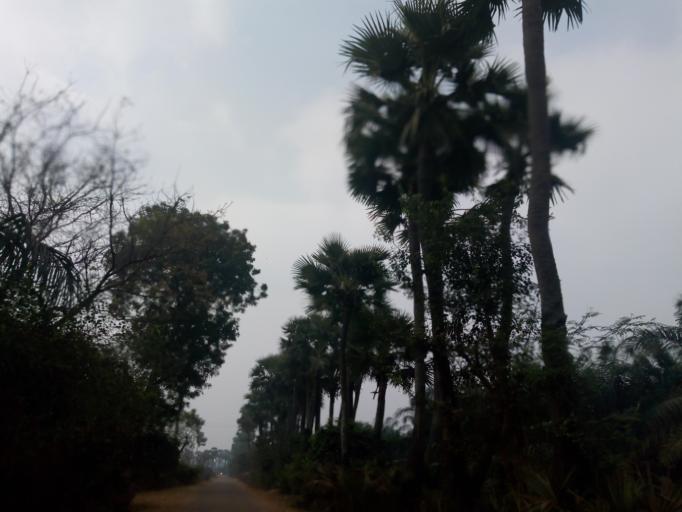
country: IN
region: Andhra Pradesh
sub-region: West Godavari
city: Tadepallegudem
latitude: 16.8584
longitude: 81.3280
